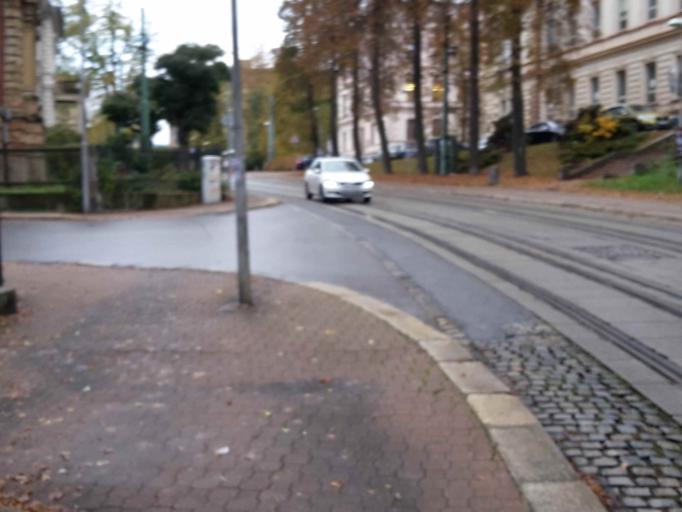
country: CZ
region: Liberecky
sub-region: Okres Liberec
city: Liberec
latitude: 50.7732
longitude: 15.0654
